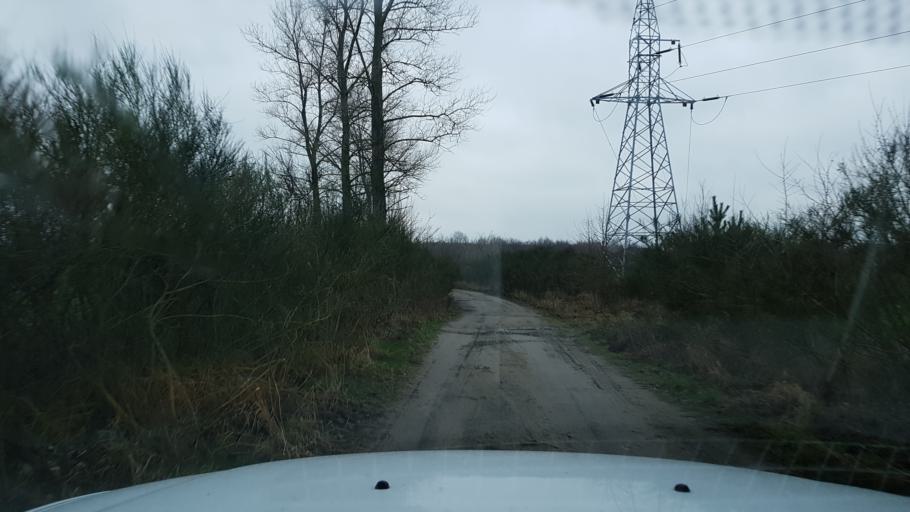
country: PL
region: West Pomeranian Voivodeship
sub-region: Powiat gryficki
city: Brojce
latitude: 53.9797
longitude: 15.3056
